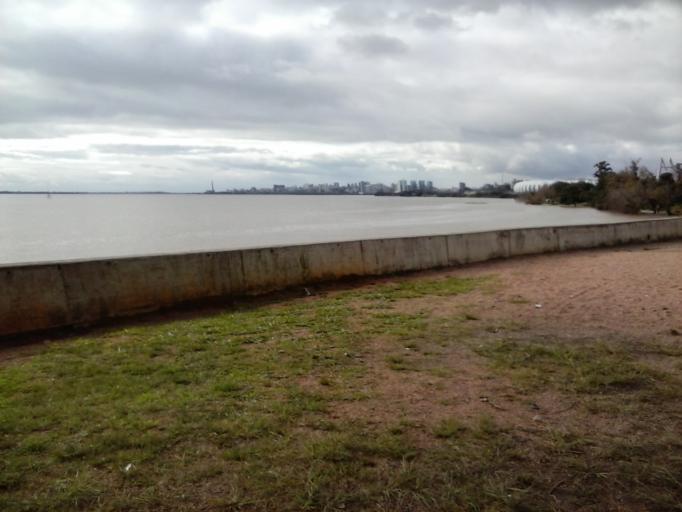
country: BR
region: Rio Grande do Sul
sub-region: Porto Alegre
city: Porto Alegre
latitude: -30.0777
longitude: -51.2457
